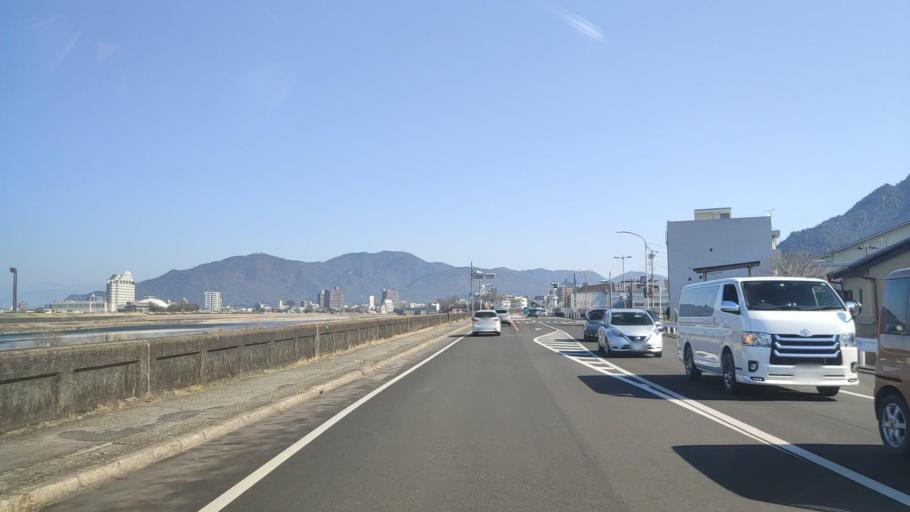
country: JP
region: Gifu
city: Gifu-shi
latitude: 35.4328
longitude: 136.7642
